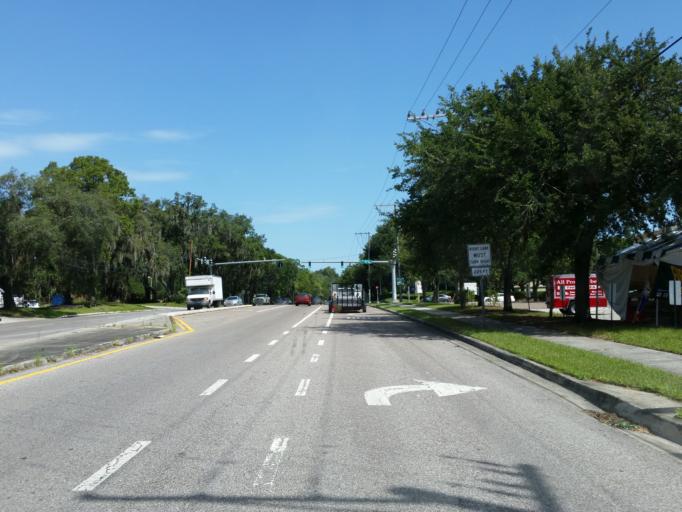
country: US
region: Florida
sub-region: Hillsborough County
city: Bloomingdale
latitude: 27.8947
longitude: -82.2446
